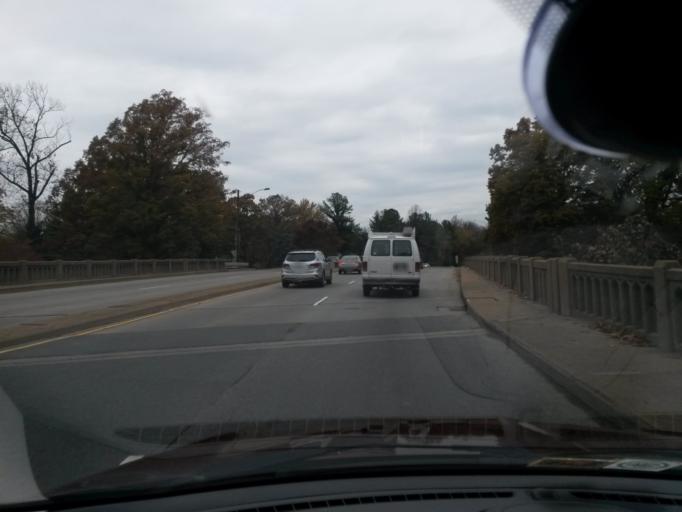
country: US
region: Virginia
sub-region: City of Charlottesville
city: Charlottesville
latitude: 38.0454
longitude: -78.4784
